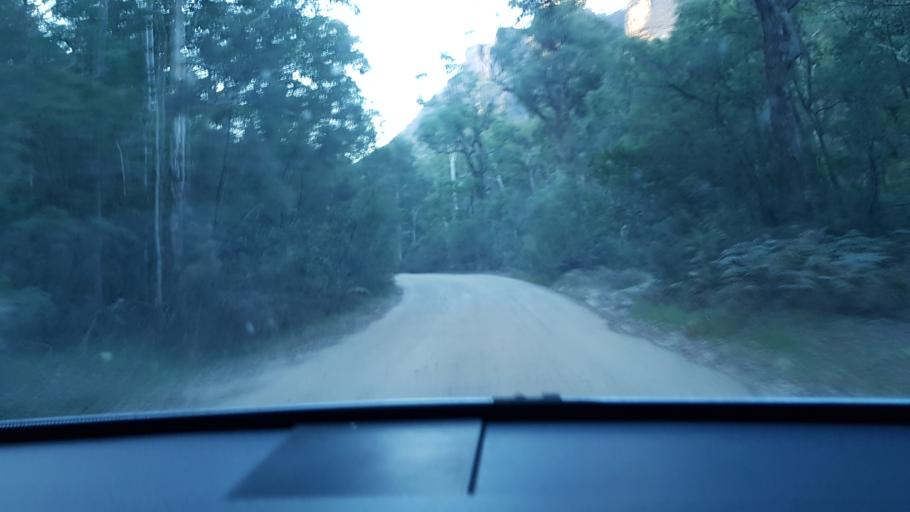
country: AU
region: New South Wales
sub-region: Lithgow
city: Lithgow
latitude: -33.1906
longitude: 150.2453
